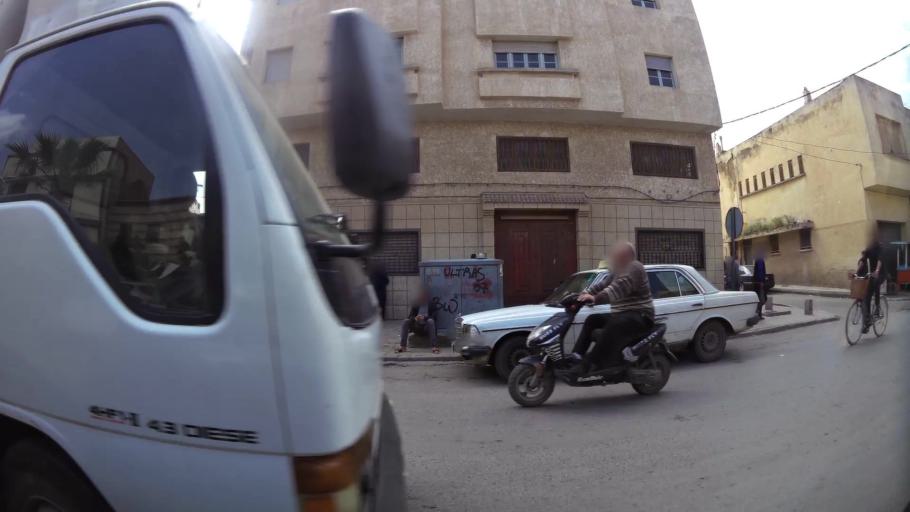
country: MA
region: Oriental
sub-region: Oujda-Angad
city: Oujda
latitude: 34.6816
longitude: -1.9065
